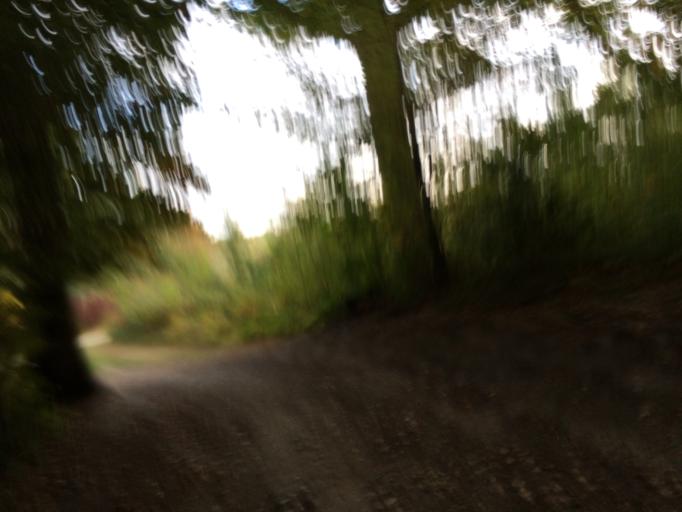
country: FR
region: Ile-de-France
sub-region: Departement de l'Essonne
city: Linas
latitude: 48.6357
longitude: 2.2549
